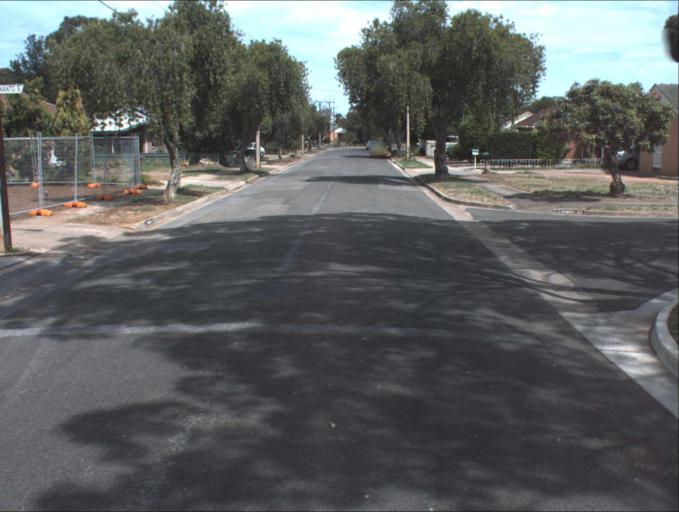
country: AU
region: South Australia
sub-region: Port Adelaide Enfield
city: Enfield
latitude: -34.8462
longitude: 138.6049
